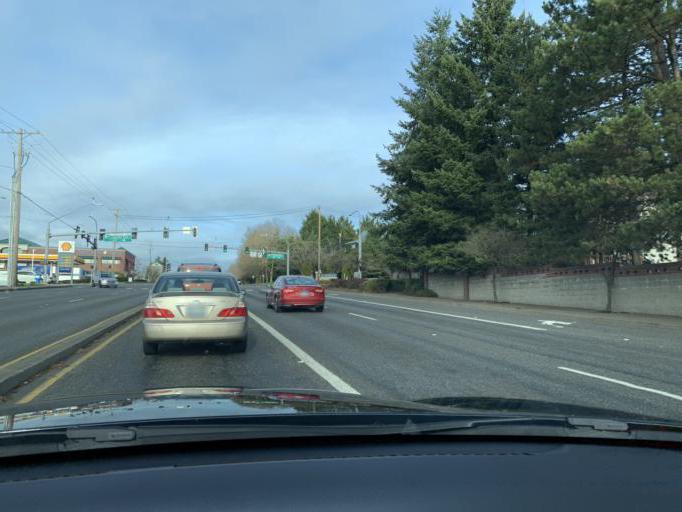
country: US
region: Washington
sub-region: Clark County
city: Mill Plain
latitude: 45.5960
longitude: -122.5039
